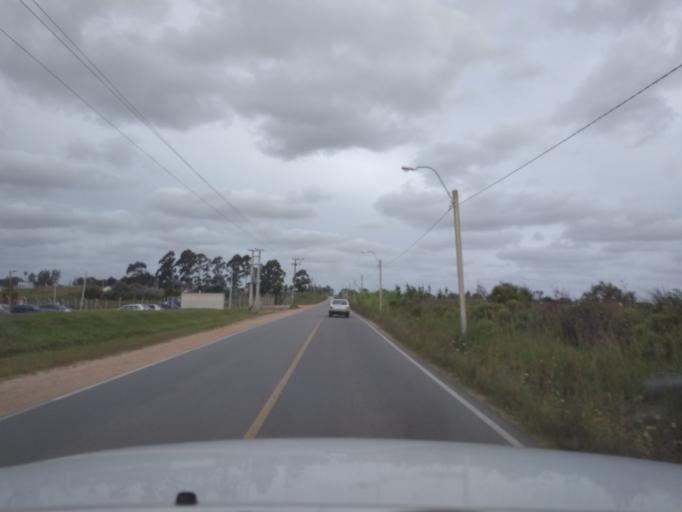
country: UY
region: Canelones
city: Colonia Nicolich
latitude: -34.7858
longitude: -56.0050
